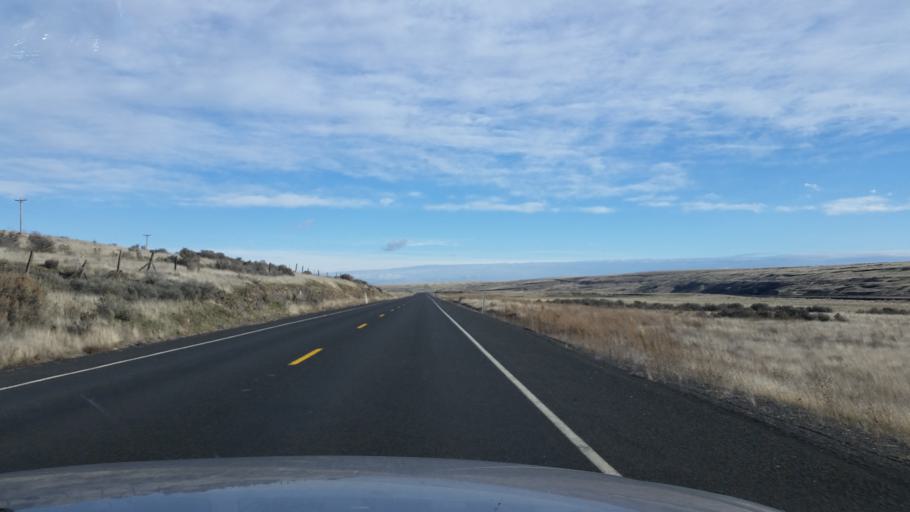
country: US
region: Washington
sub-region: Adams County
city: Ritzville
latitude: 47.3477
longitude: -118.5728
